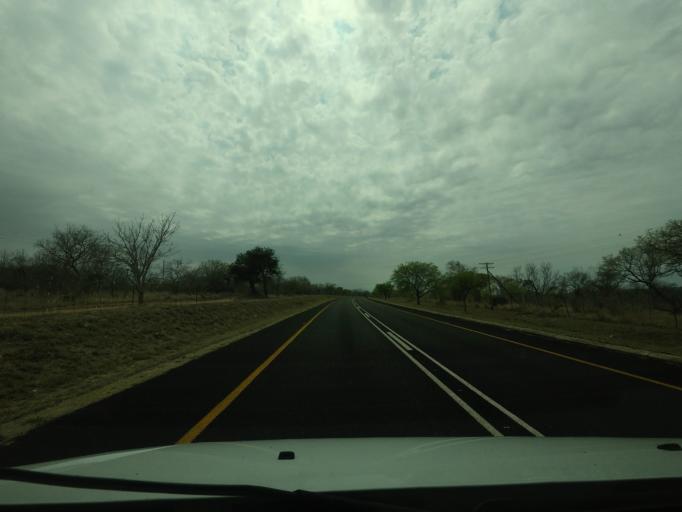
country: ZA
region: Limpopo
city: Thulamahashi
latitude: -24.5549
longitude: 31.1826
